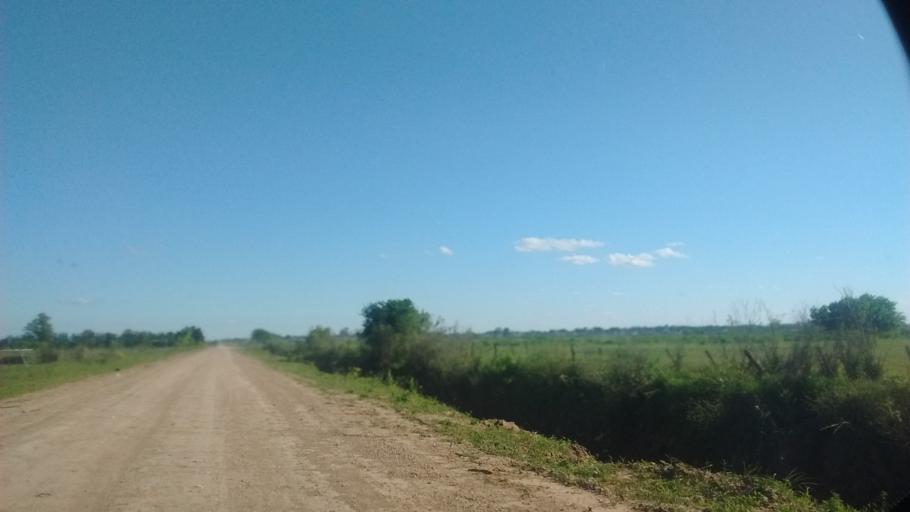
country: AR
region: Santa Fe
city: Funes
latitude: -32.8894
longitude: -60.7979
